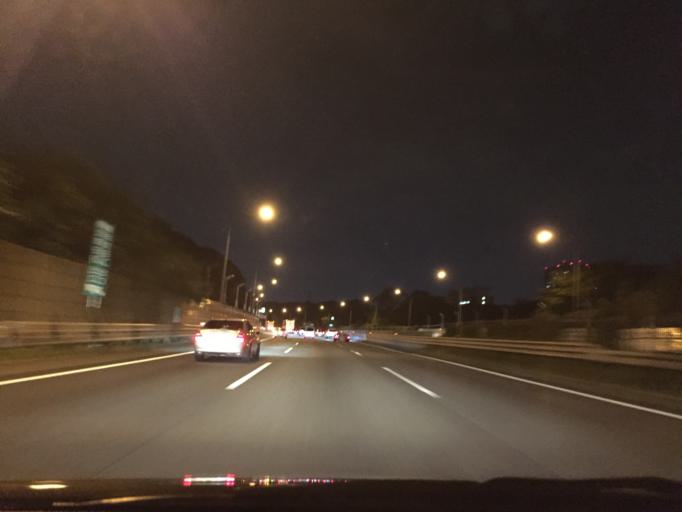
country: JP
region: Tokyo
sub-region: Machida-shi
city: Machida
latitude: 35.5138
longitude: 139.4905
